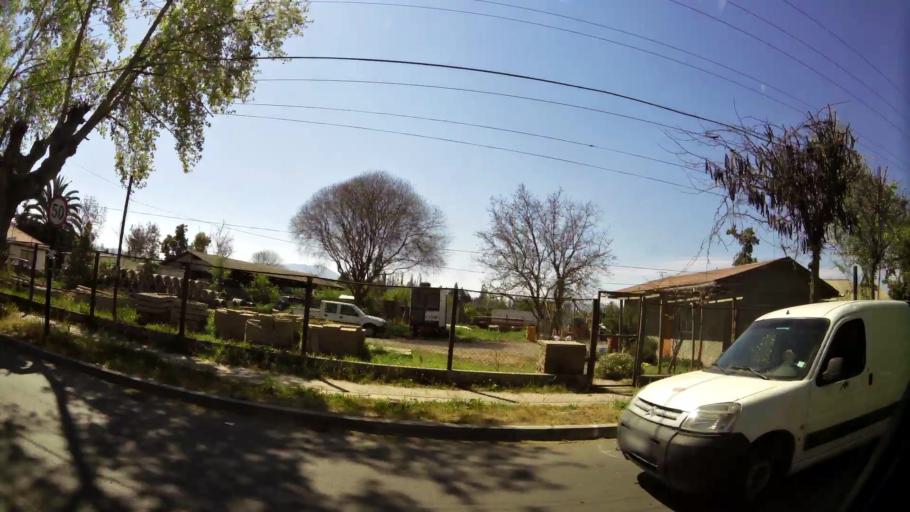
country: CL
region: Santiago Metropolitan
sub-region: Provincia de Talagante
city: Penaflor
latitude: -33.5970
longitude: -70.8824
